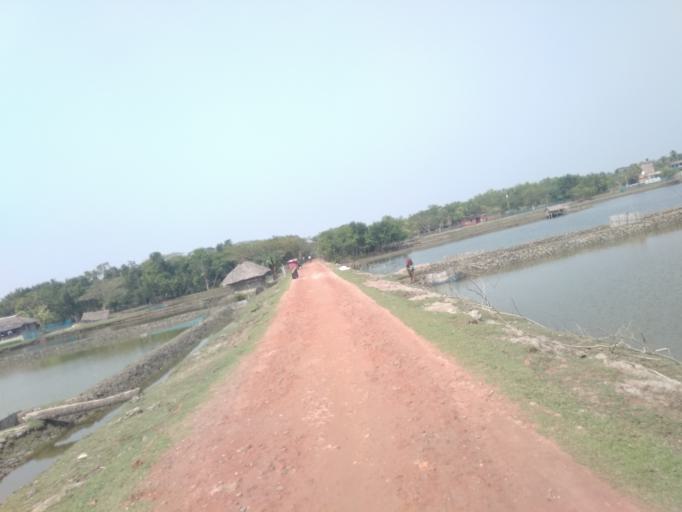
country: IN
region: West Bengal
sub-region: North 24 Parganas
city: Taki
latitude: 22.2968
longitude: 89.2702
